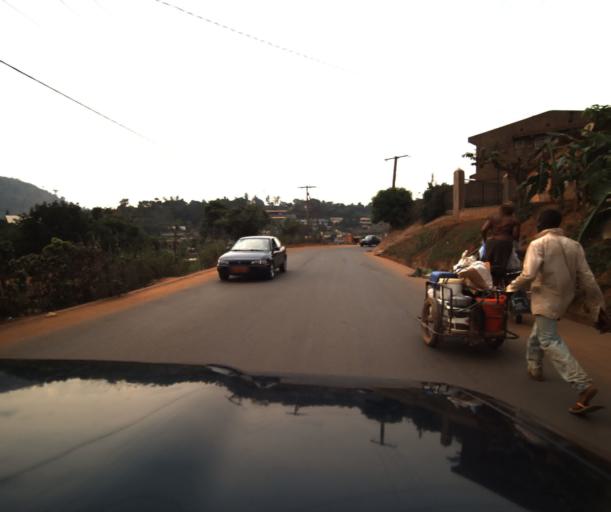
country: CM
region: Centre
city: Yaounde
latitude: 3.8458
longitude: 11.4790
